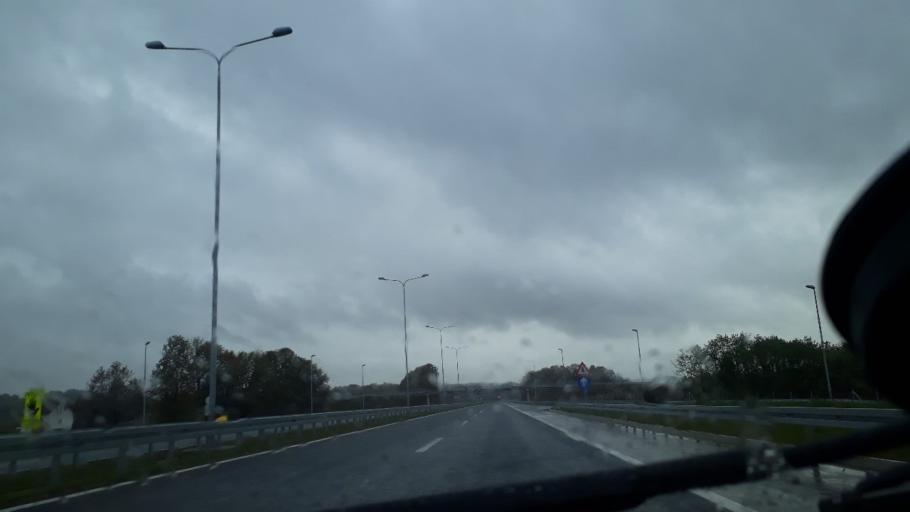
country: BA
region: Republika Srpska
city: Stanari
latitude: 44.8147
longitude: 17.8978
